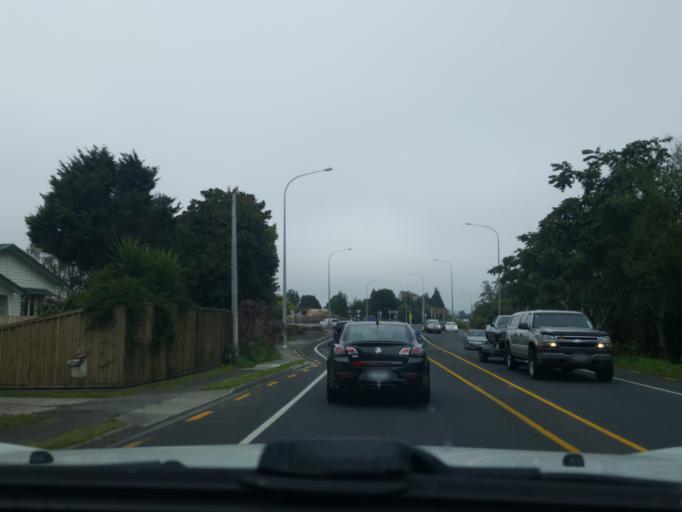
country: NZ
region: Waikato
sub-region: Waikato District
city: Ngaruawahia
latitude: -37.6106
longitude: 175.1858
